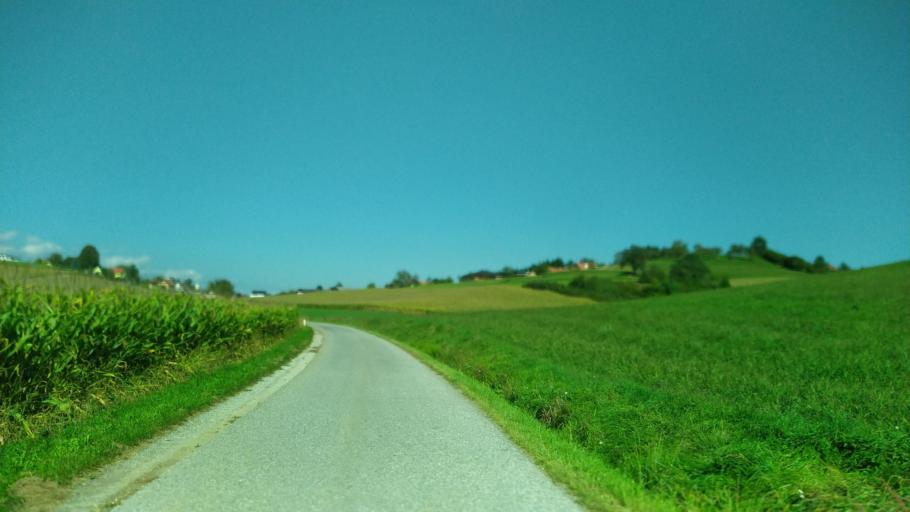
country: AT
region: Styria
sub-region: Politischer Bezirk Deutschlandsberg
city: Wettmannstatten
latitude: 46.8187
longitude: 15.3764
